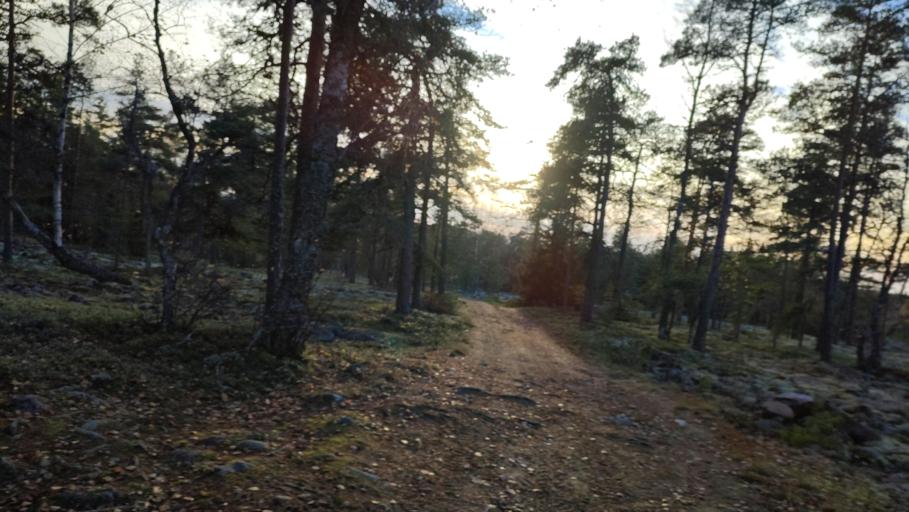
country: FI
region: Southern Ostrobothnia
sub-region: Suupohja
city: Karijoki
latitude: 62.2840
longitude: 21.6458
